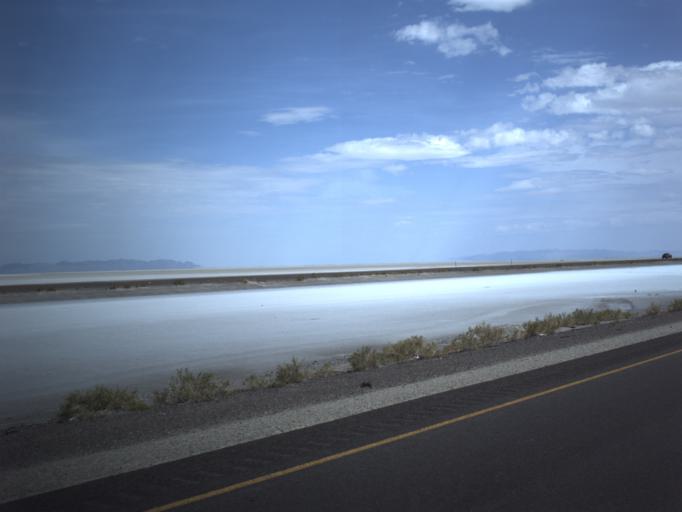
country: US
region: Utah
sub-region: Tooele County
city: Wendover
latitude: 40.7356
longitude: -113.7111
